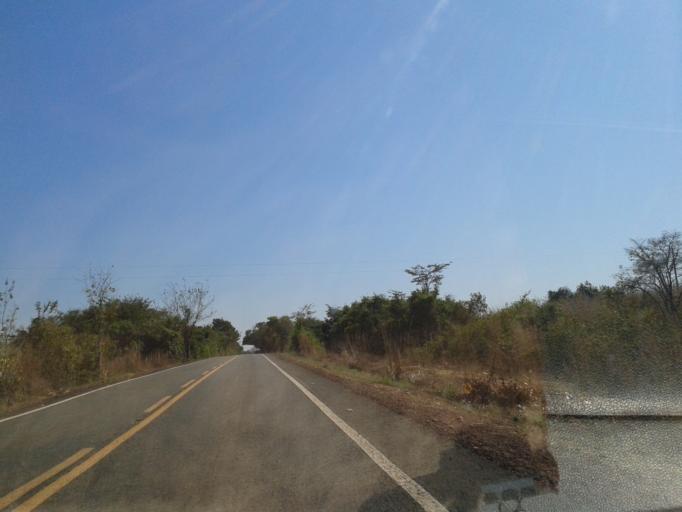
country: BR
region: Goias
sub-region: Sao Miguel Do Araguaia
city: Sao Miguel do Araguaia
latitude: -13.8599
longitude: -50.3343
